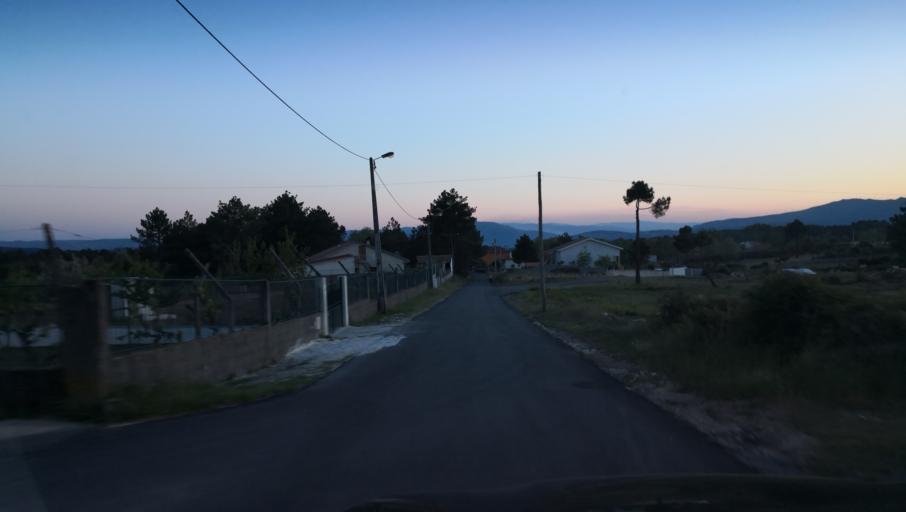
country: PT
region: Vila Real
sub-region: Vila Real
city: Vila Real
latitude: 41.3003
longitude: -7.6710
